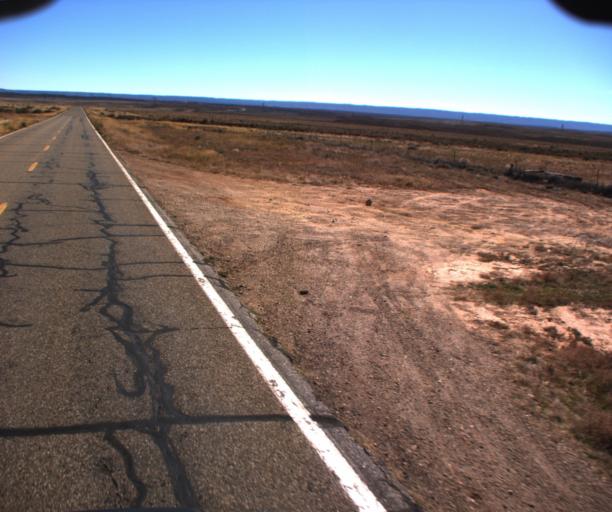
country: US
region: Arizona
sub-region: Coconino County
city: Fredonia
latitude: 36.9230
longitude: -112.4504
